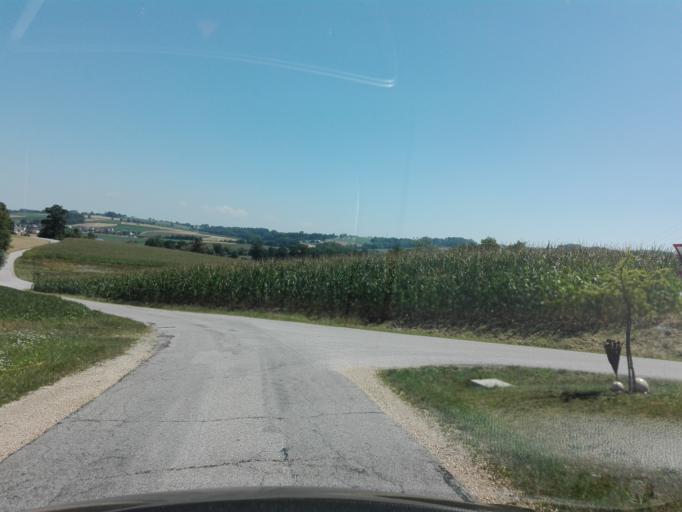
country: AT
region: Upper Austria
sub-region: Politischer Bezirk Urfahr-Umgebung
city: Engerwitzdorf
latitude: 48.2914
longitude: 14.4650
